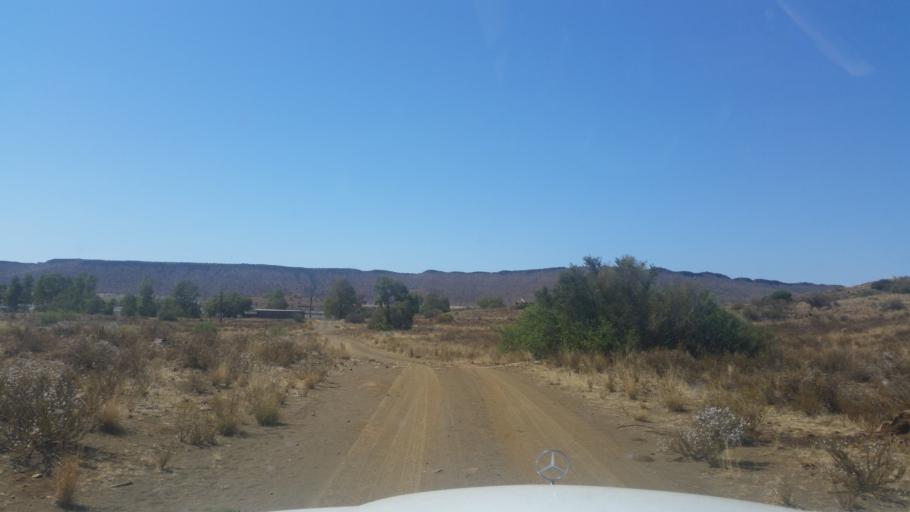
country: ZA
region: Eastern Cape
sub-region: Joe Gqabi District Municipality
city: Burgersdorp
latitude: -30.6947
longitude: 25.7805
